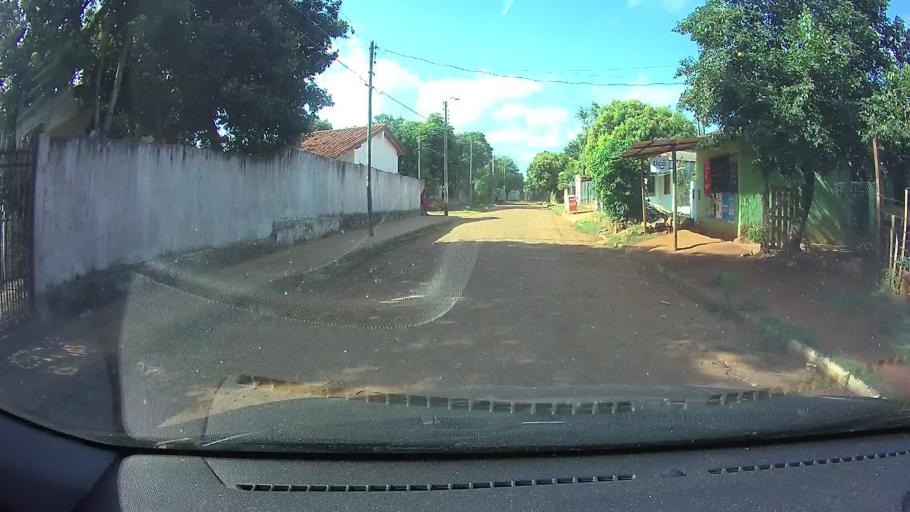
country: PY
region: Central
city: Limpio
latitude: -25.2435
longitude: -57.4671
